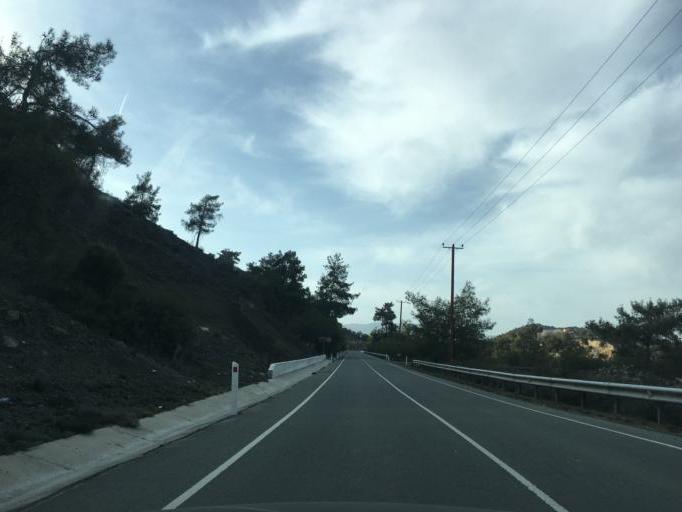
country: CY
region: Limassol
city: Pelendri
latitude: 34.8272
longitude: 32.9644
